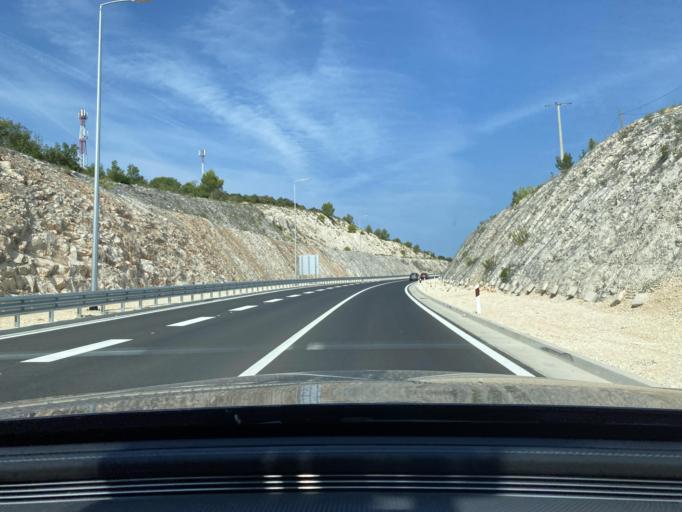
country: HR
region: Dubrovacko-Neretvanska
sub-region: Grad Dubrovnik
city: Opuzen
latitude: 42.9445
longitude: 17.5399
